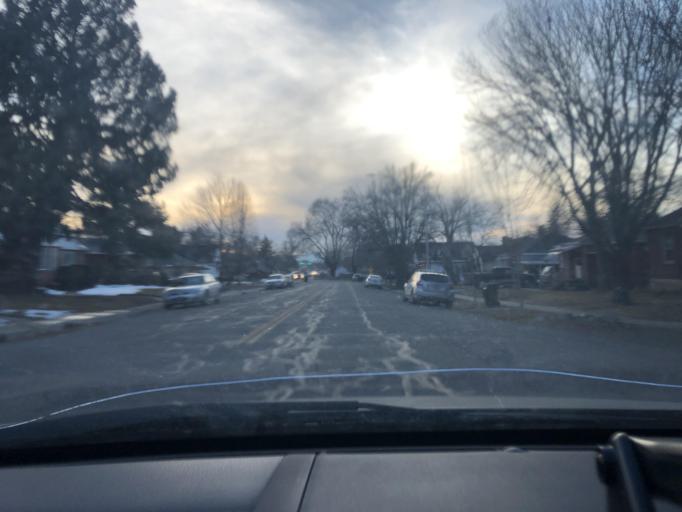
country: US
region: Utah
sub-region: Utah County
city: Provo
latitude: 40.2298
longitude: -111.6401
